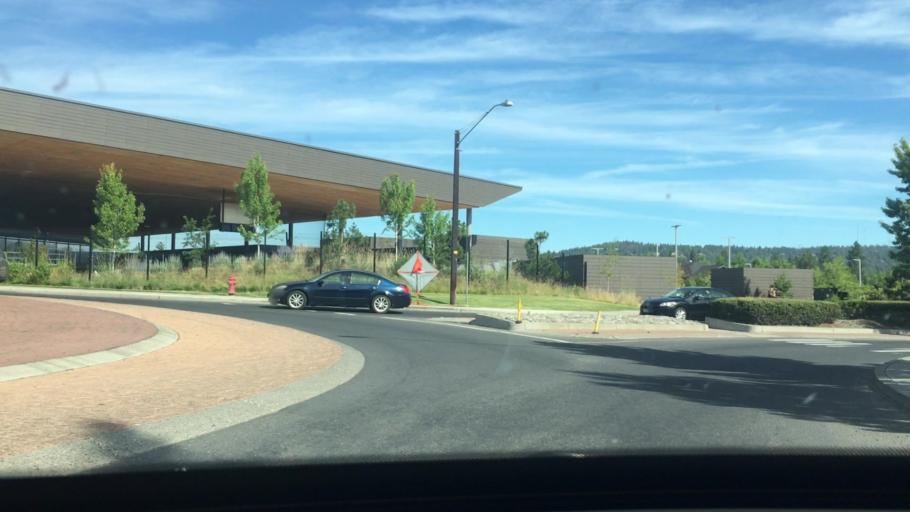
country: US
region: Oregon
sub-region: Deschutes County
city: Bend
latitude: 44.0478
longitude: -121.3228
